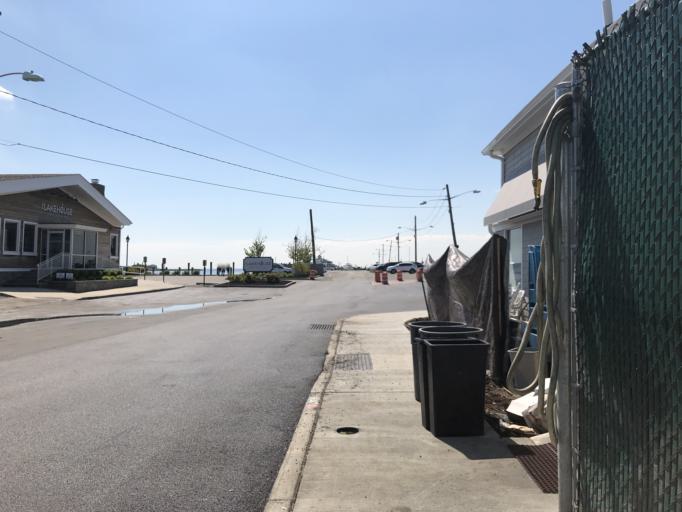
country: US
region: New York
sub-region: Suffolk County
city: Bay Shore
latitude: 40.7154
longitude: -73.2411
